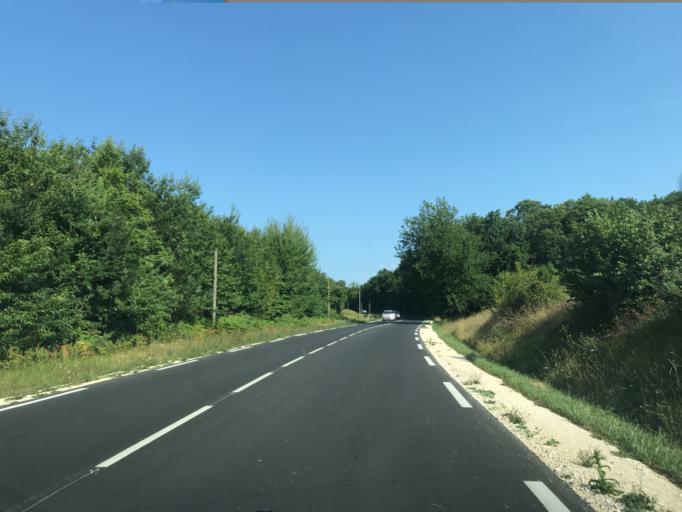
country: FR
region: Aquitaine
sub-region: Departement de la Dordogne
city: Montignac
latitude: 45.0175
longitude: 1.2361
